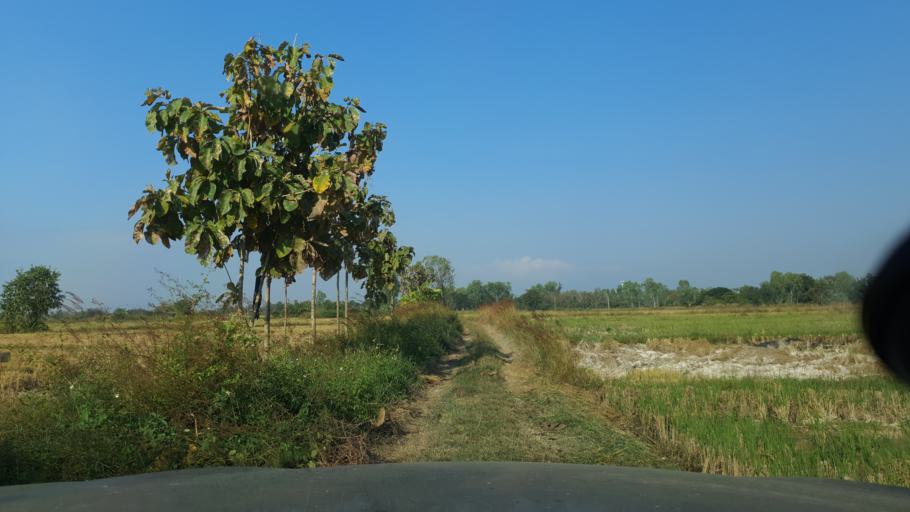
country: TH
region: Lamphun
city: Ban Thi
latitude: 18.6762
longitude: 99.1340
